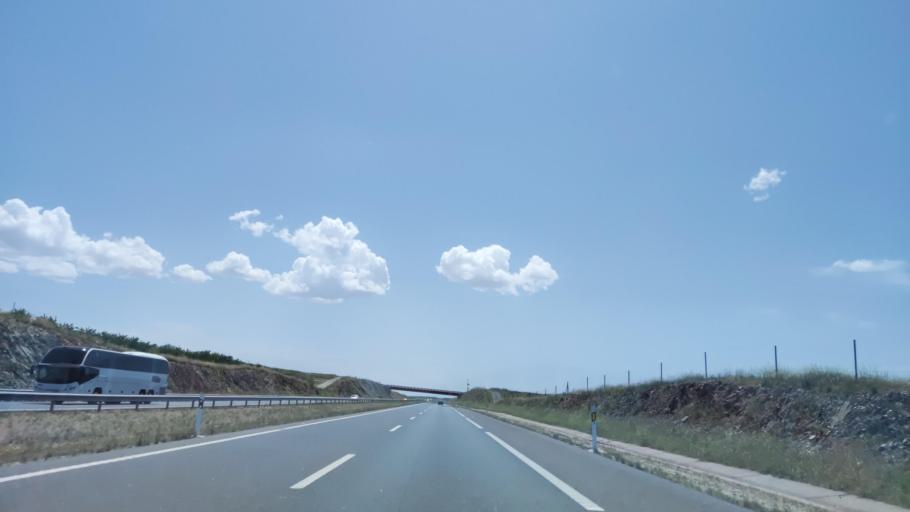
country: ES
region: Castille-La Mancha
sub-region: Province of Toledo
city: Villaminaya
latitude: 39.7394
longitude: -3.8599
